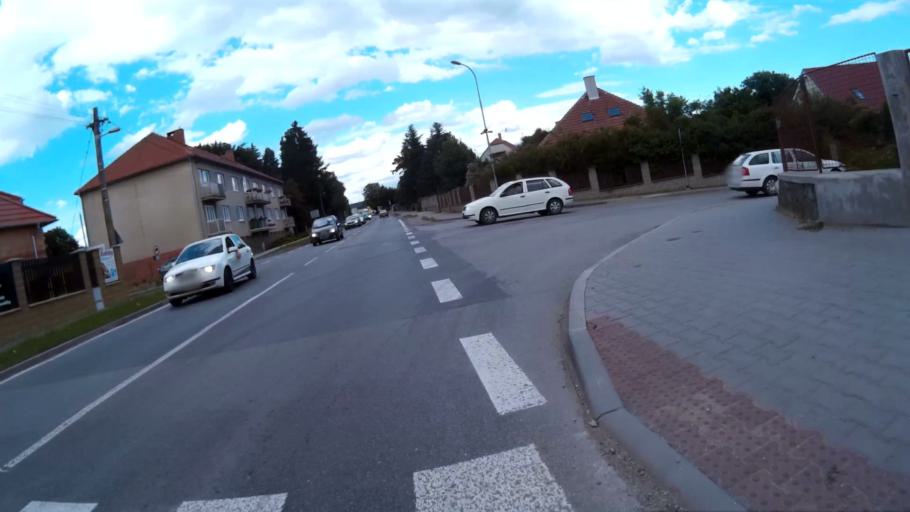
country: CZ
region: South Moravian
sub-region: Okres Brno-Venkov
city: Rosice
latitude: 49.1830
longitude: 16.3988
